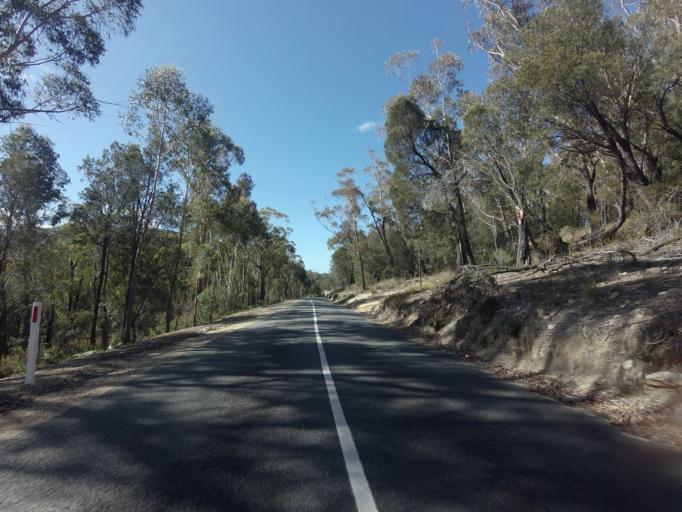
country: AU
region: Tasmania
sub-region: Break O'Day
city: St Helens
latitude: -41.6633
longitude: 148.2689
